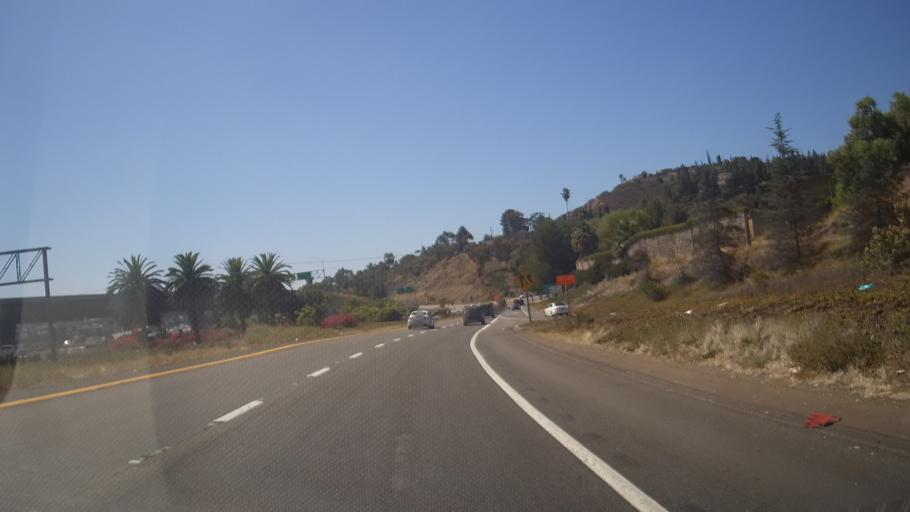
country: US
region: California
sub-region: San Diego County
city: Spring Valley
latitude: 32.7552
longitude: -117.0103
